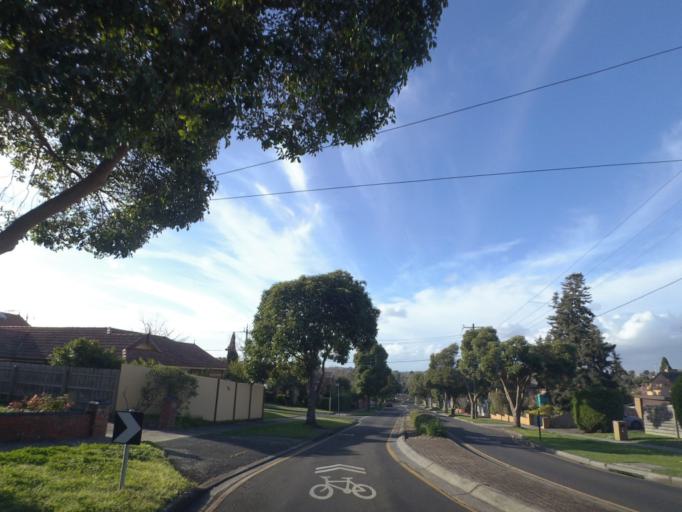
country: AU
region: Victoria
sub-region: Whitehorse
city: Box Hill
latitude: -37.8116
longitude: 145.1320
